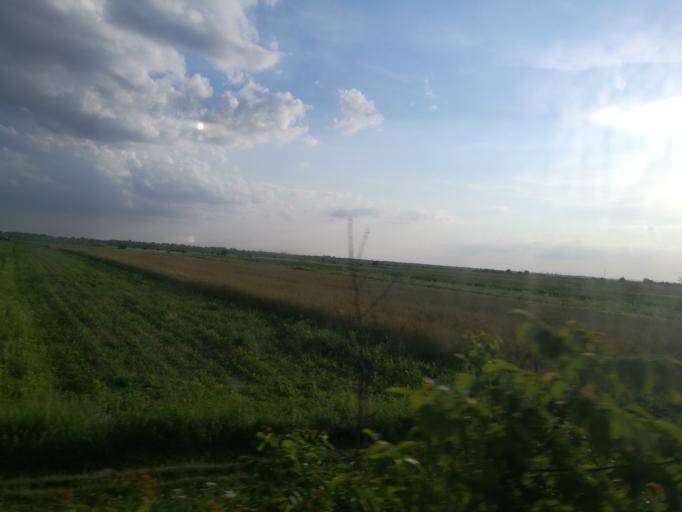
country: RO
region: Arges
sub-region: Comuna Leordeni
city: Leordeni
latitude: 44.7932
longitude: 25.1048
